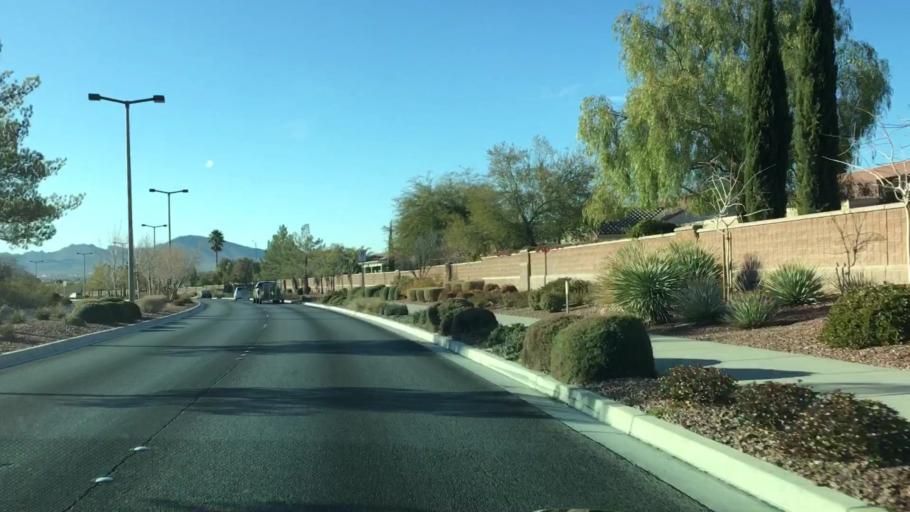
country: US
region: Nevada
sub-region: Clark County
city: Whitney
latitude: 35.9667
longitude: -115.1208
